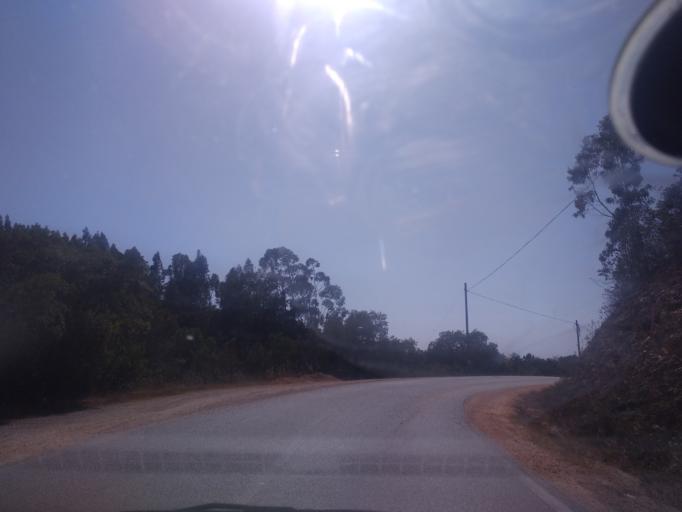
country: PT
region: Faro
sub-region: Aljezur
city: Aljezur
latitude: 37.2221
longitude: -8.8036
